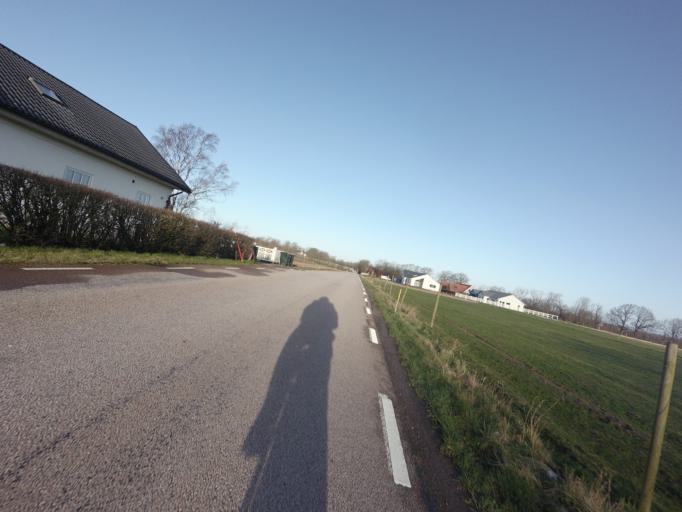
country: SE
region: Skane
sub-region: Helsingborg
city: Odakra
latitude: 56.1146
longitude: 12.6816
